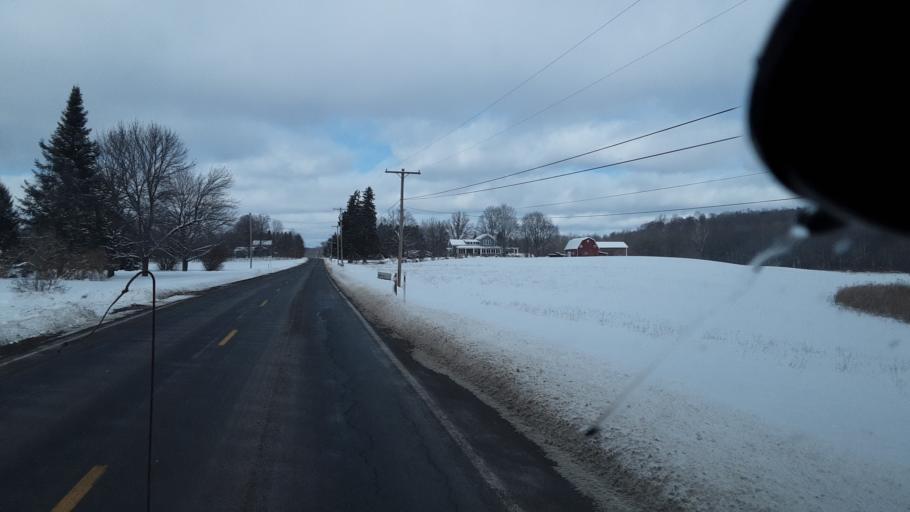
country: US
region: New York
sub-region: Wayne County
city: Newark
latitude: 43.0940
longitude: -77.0537
